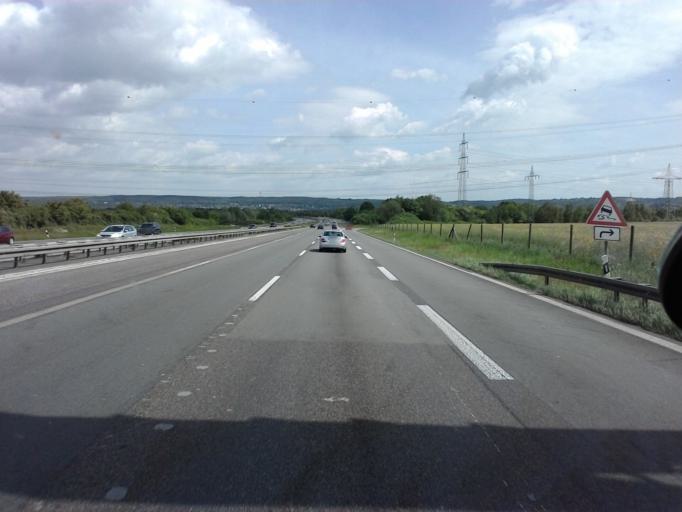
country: DE
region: North Rhine-Westphalia
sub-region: Regierungsbezirk Koln
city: Stossdorf
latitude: 50.7718
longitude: 7.2368
